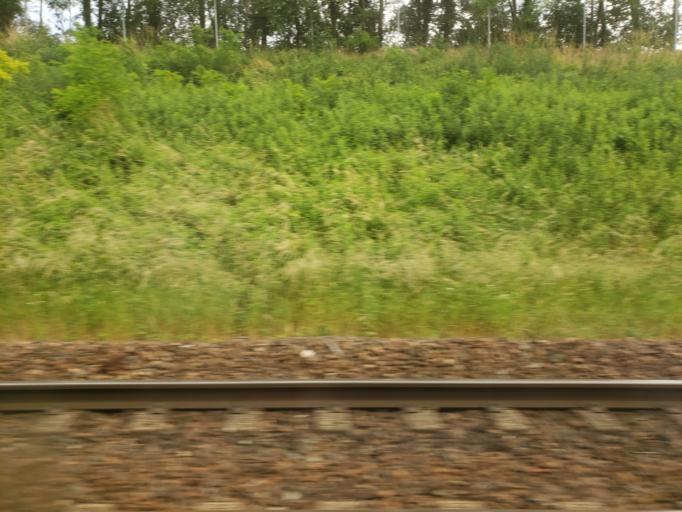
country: FR
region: Rhone-Alpes
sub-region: Departement du Rhone
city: Sathonay-Village
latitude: 45.8271
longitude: 4.8882
